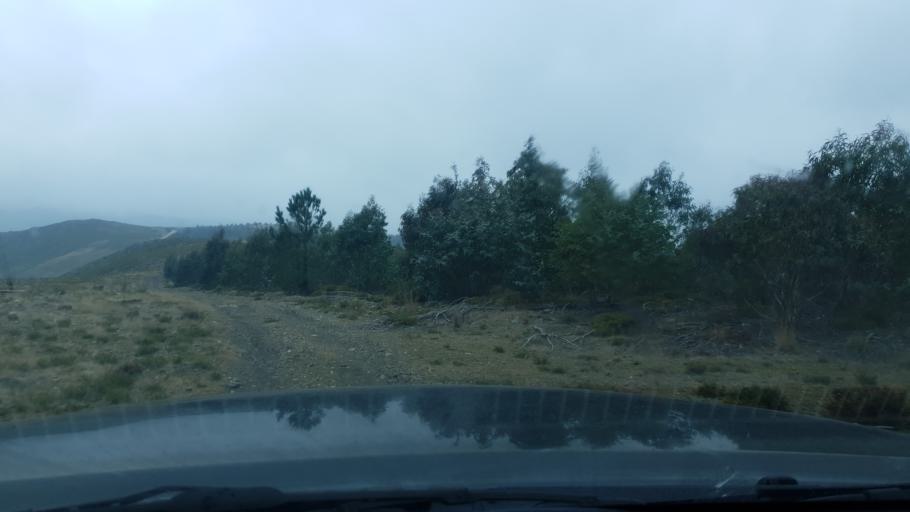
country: PT
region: Viseu
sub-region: Sao Pedro do Sul
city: Sao Pedro do Sul
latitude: 40.8608
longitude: -8.0953
